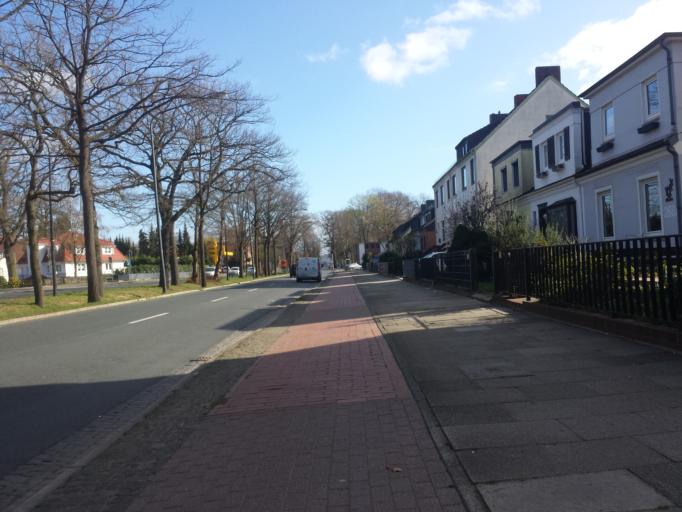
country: DE
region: Lower Saxony
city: Lilienthal
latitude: 53.0757
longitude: 8.8815
